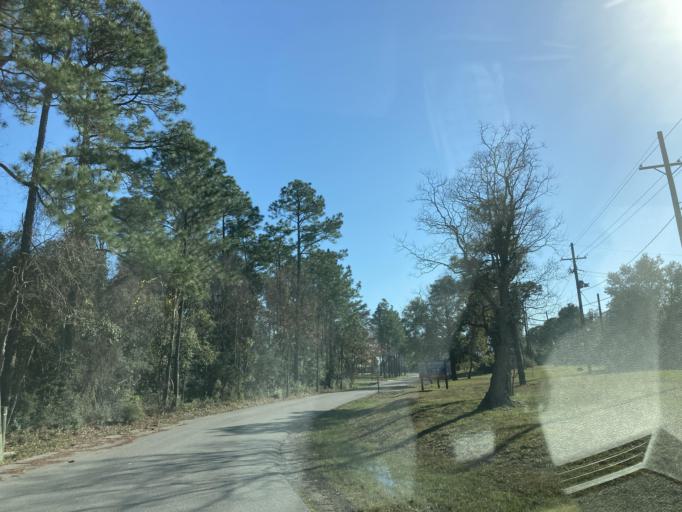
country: US
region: Mississippi
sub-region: Harrison County
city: West Gulfport
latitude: 30.4313
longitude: -89.0612
